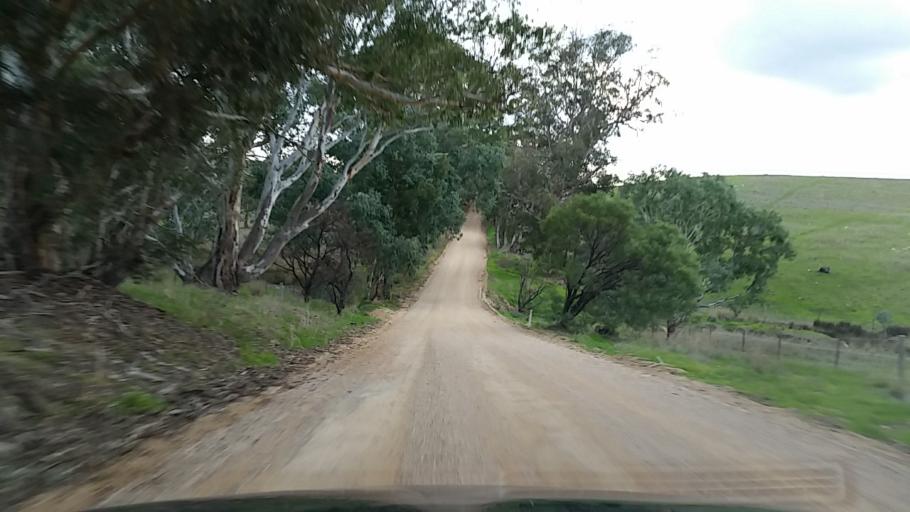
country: AU
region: South Australia
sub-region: Mount Barker
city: Nairne
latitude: -34.9595
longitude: 139.0215
